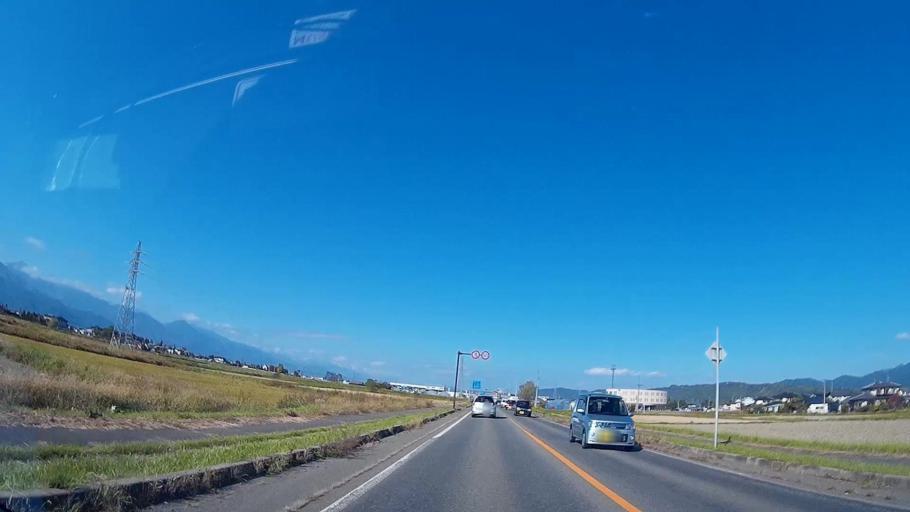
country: JP
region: Nagano
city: Matsumoto
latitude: 36.2228
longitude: 137.9334
